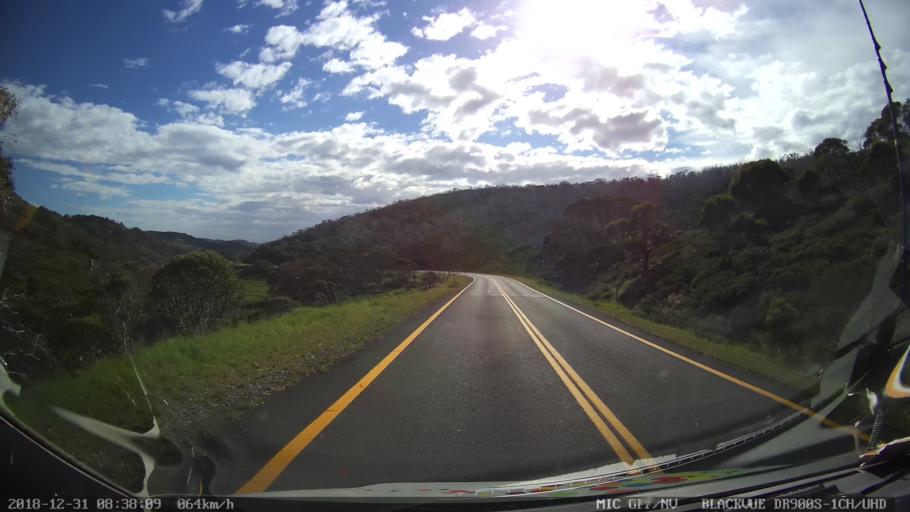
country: AU
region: New South Wales
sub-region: Snowy River
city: Jindabyne
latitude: -36.4159
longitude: 148.3924
